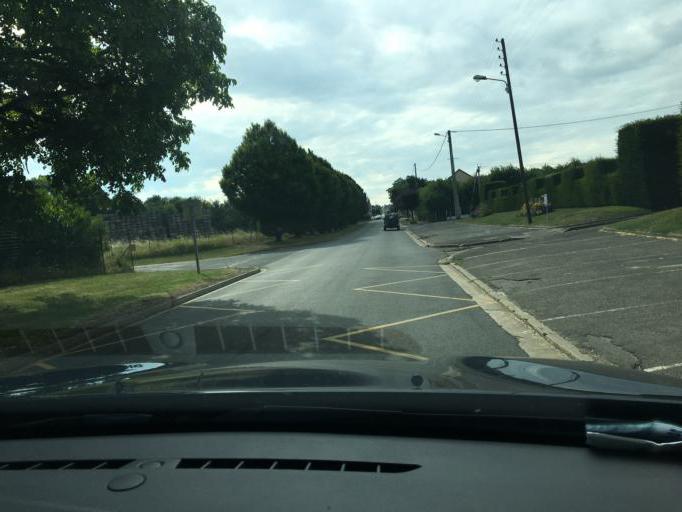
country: FR
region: Centre
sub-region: Departement du Cher
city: Rians
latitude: 47.1982
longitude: 2.5826
